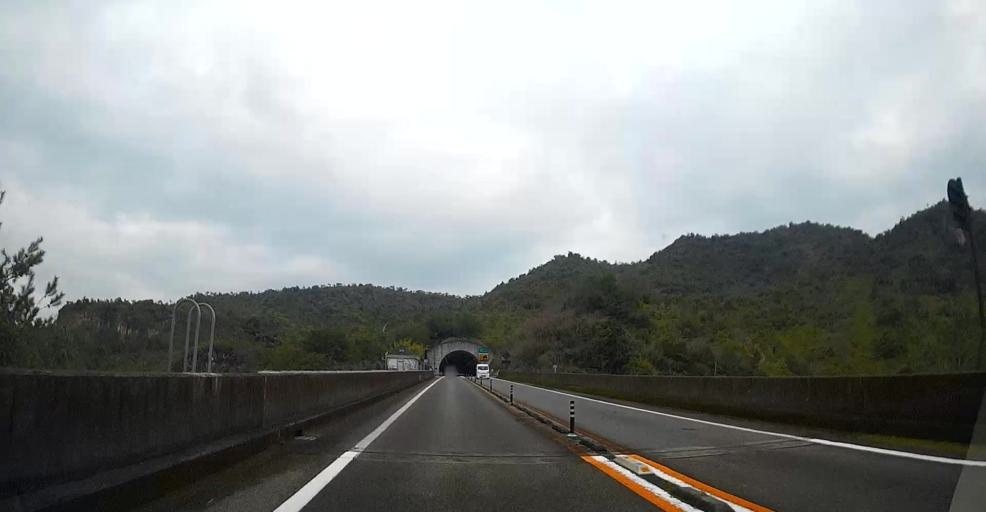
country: JP
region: Kumamoto
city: Yatsushiro
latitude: 32.5075
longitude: 130.4048
